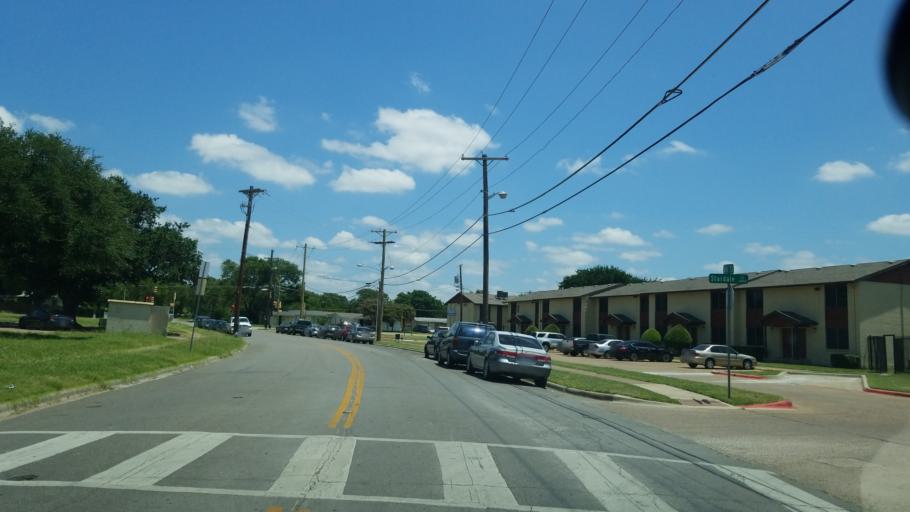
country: US
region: Texas
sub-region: Dallas County
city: Balch Springs
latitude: 32.7384
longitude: -96.7017
